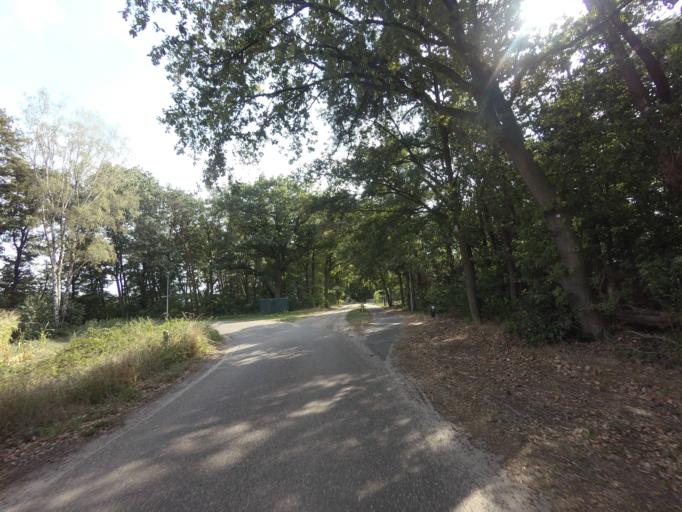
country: NL
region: North Brabant
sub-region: Gemeente Someren
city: Someren
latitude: 51.4061
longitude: 5.6759
